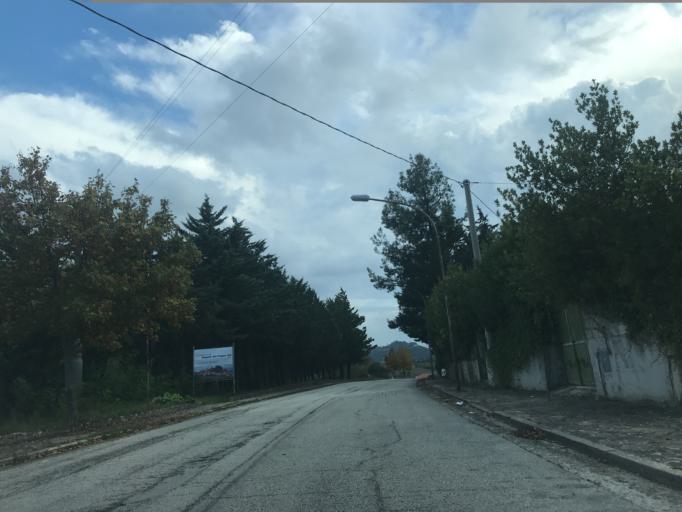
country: IT
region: Molise
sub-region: Provincia di Isernia
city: Bagnoli del Trigno
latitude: 41.6989
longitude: 14.4606
